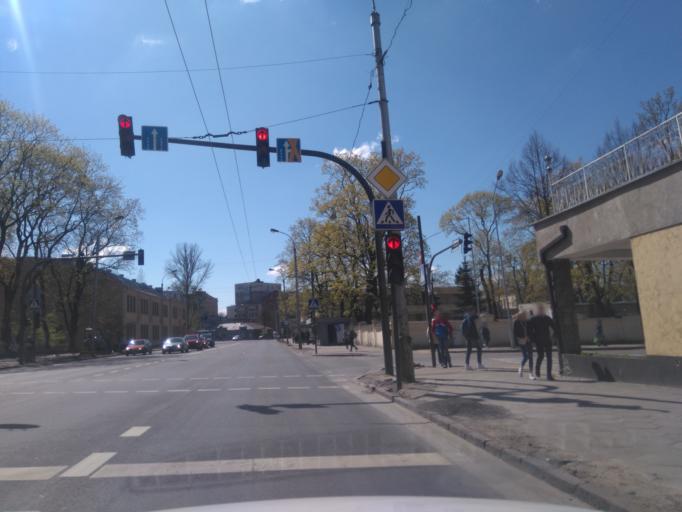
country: LT
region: Kauno apskritis
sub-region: Kaunas
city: Kaunas
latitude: 54.8923
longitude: 23.9247
